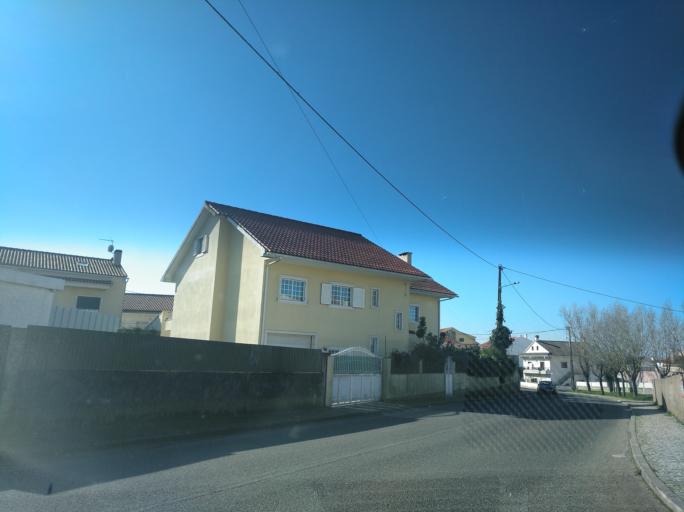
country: PT
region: Lisbon
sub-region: Odivelas
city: Canecas
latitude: 38.8047
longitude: -9.2171
